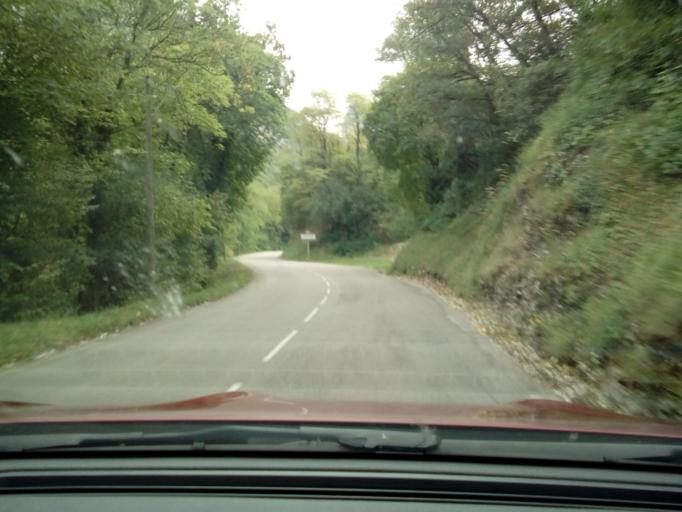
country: FR
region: Rhone-Alpes
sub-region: Departement de l'Isere
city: Pont-en-Royans
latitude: 45.0571
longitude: 5.3406
